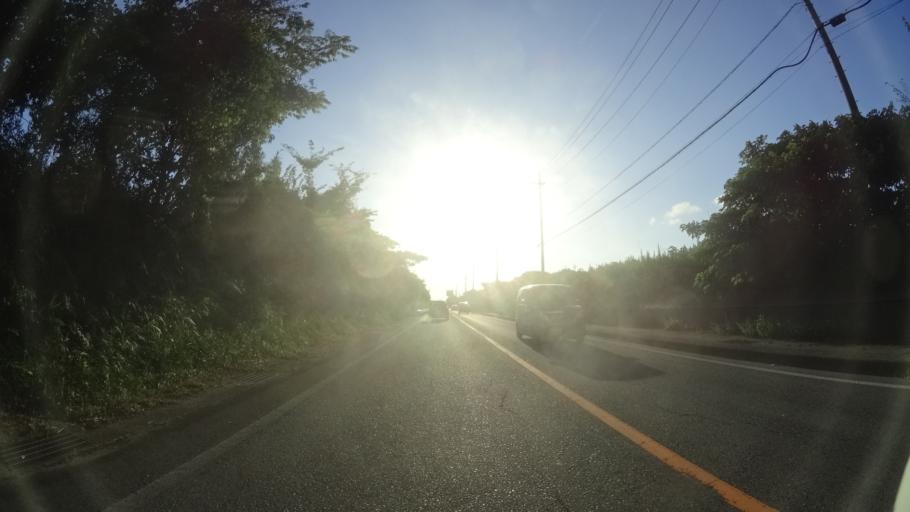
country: JP
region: Tottori
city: Yonago
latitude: 35.5139
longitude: 133.5151
